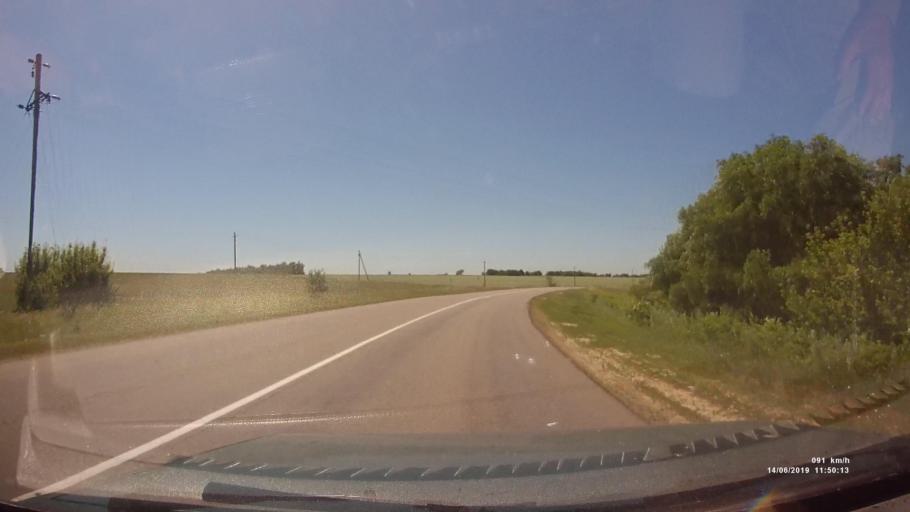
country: RU
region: Rostov
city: Kazanskaya
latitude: 49.8469
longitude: 41.2699
